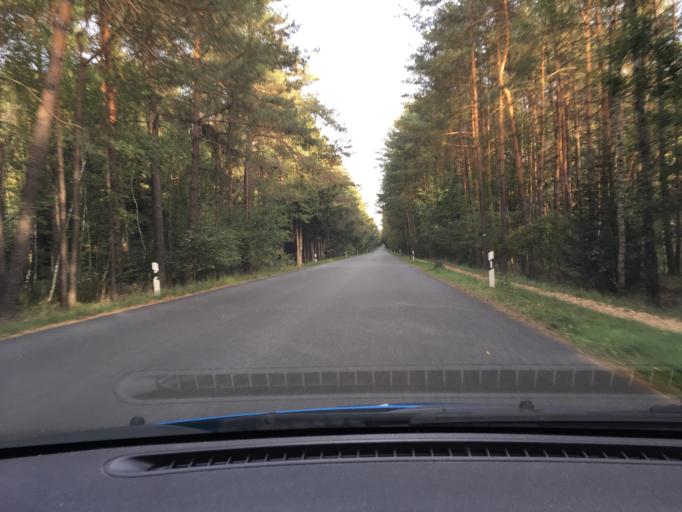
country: DE
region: Lower Saxony
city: Wietzendorf
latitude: 52.9685
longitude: 9.9402
